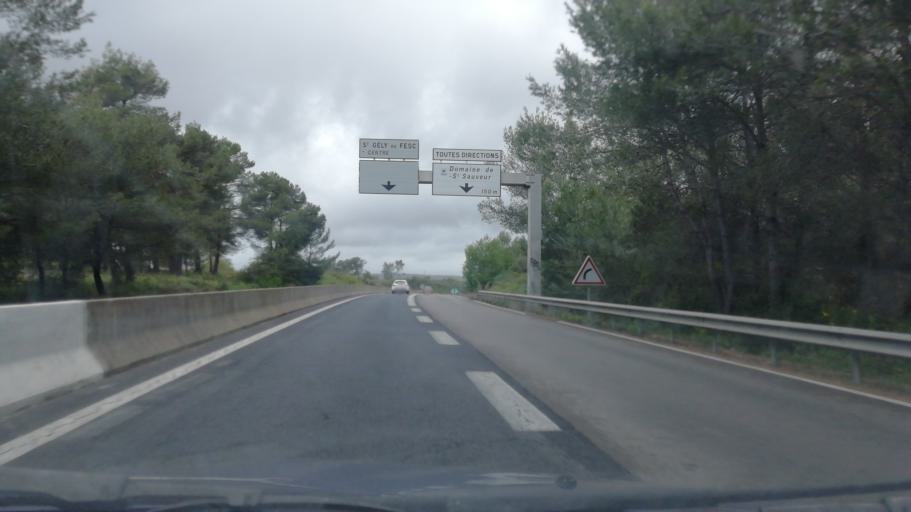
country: FR
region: Languedoc-Roussillon
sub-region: Departement de l'Herault
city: Saint-Clement-de-Riviere
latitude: 43.6715
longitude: 3.8220
